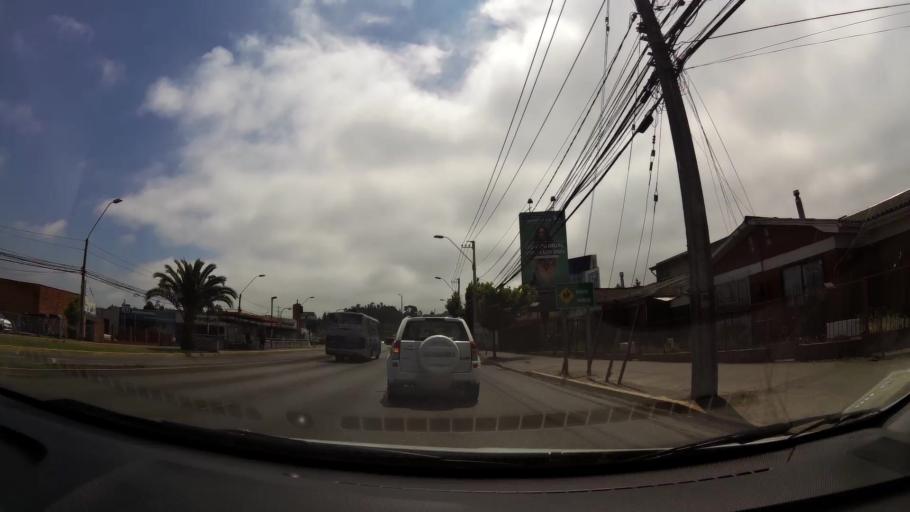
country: CL
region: Biobio
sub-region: Provincia de Concepcion
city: Concepcion
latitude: -36.8019
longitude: -73.0560
